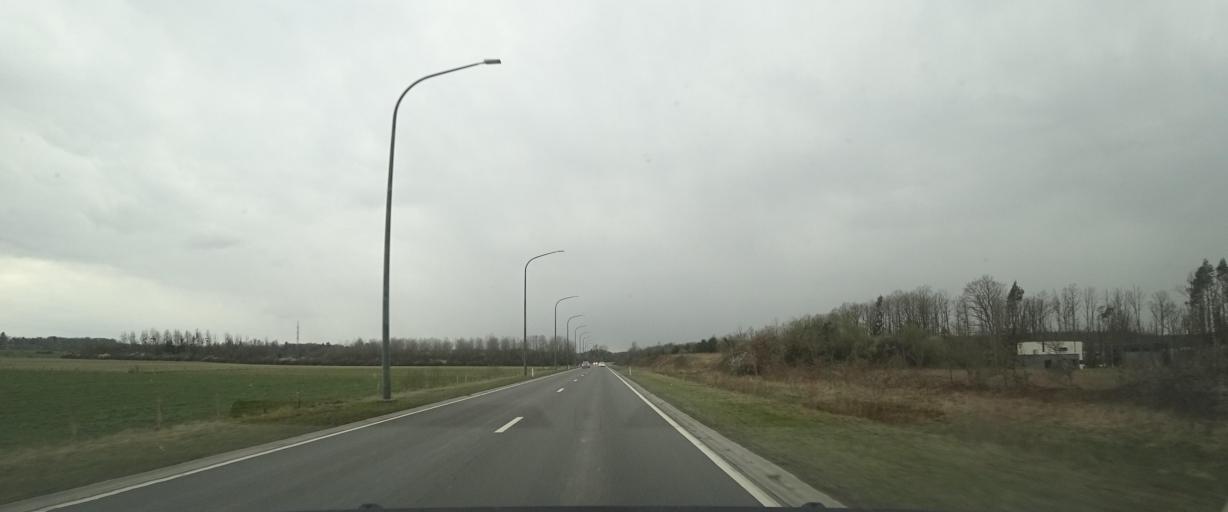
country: BE
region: Wallonia
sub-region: Province du Luxembourg
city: Marche-en-Famenne
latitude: 50.2412
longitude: 5.3313
